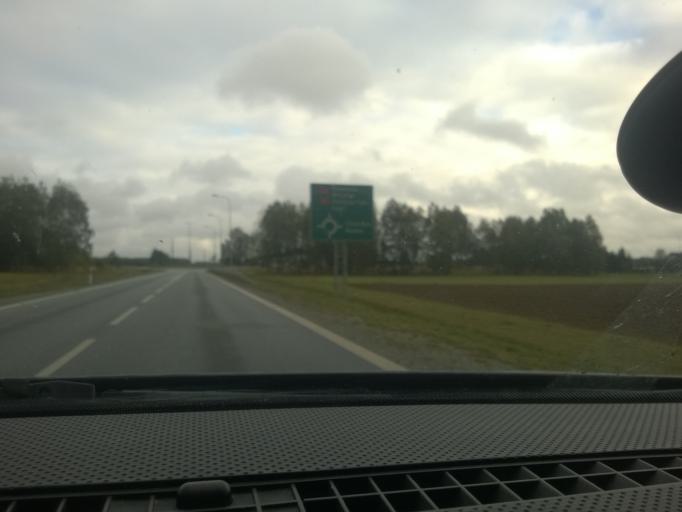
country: PL
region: Lodz Voivodeship
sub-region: Powiat sieradzki
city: Sieradz
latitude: 51.5817
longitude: 18.6703
